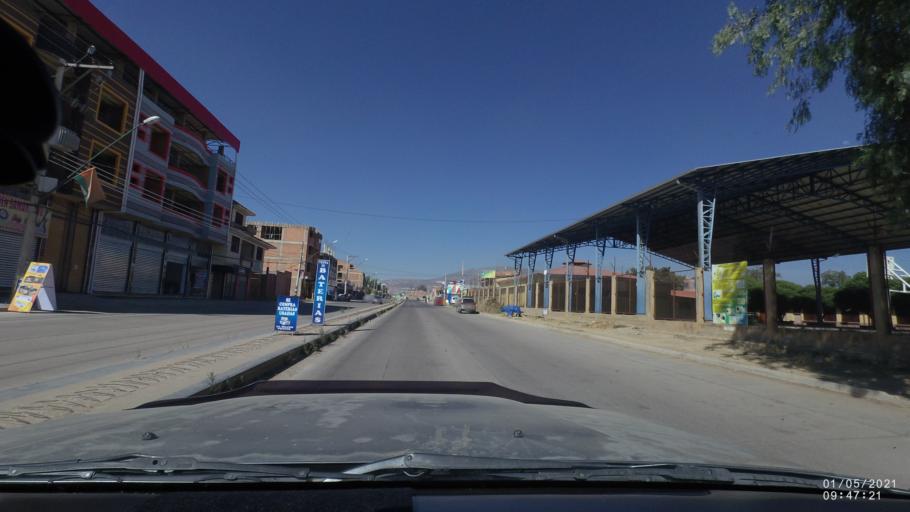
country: BO
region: Cochabamba
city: Cochabamba
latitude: -17.4453
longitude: -66.1647
